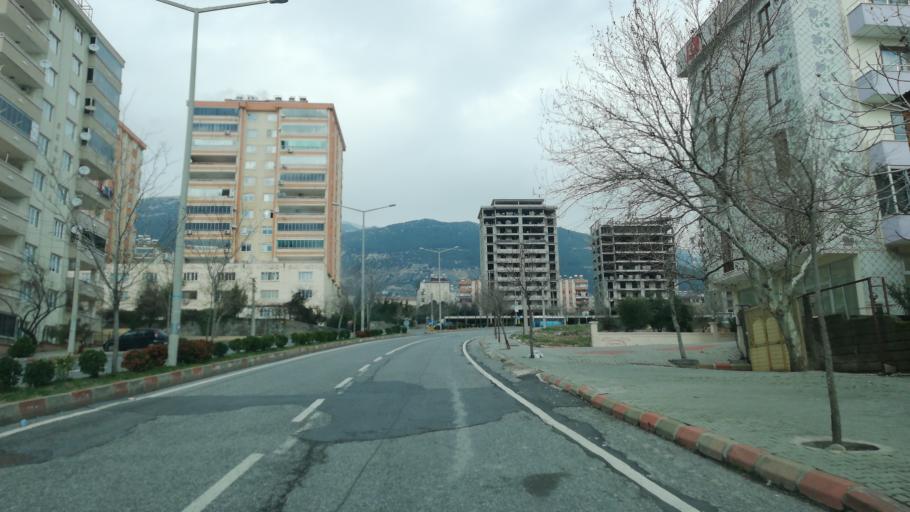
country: TR
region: Kahramanmaras
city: Kahramanmaras
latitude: 37.5910
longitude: 36.8635
